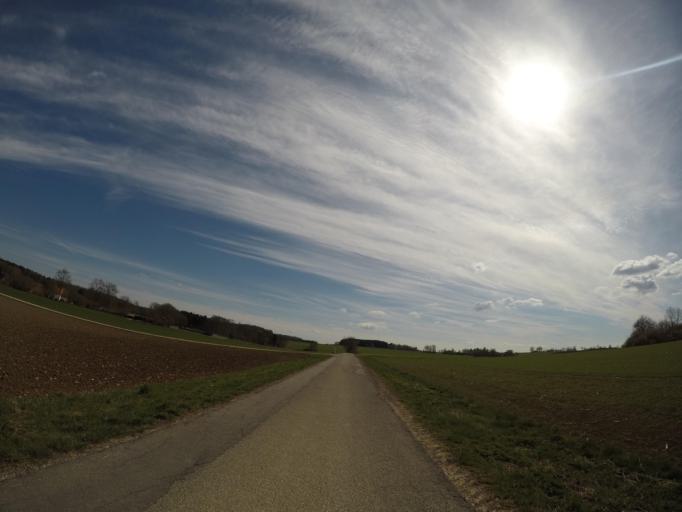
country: DE
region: Baden-Wuerttemberg
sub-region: Tuebingen Region
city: Mehrstetten
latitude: 48.3455
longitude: 9.5692
